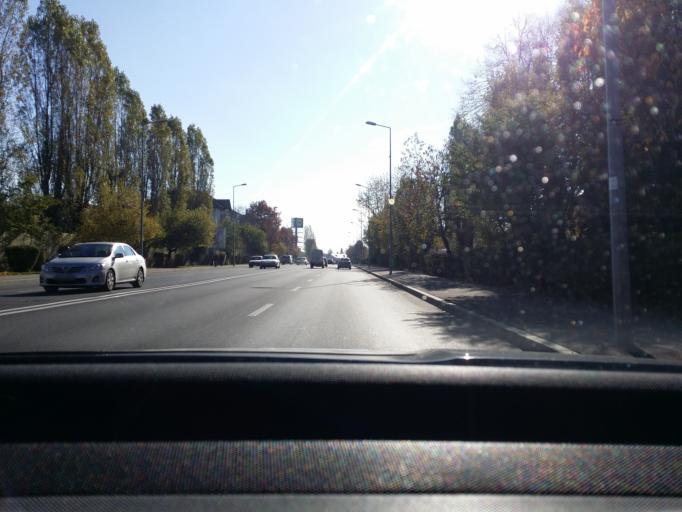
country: RO
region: Prahova
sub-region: Municipiul Campina
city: Campina
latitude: 45.1172
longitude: 25.7421
